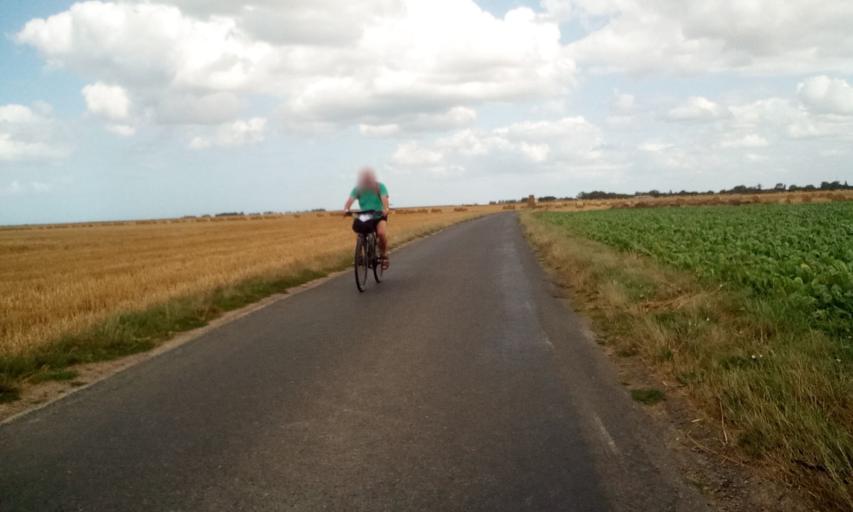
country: FR
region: Lower Normandy
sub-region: Departement du Calvados
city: Ver-sur-Mer
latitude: 49.3133
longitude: -0.5350
